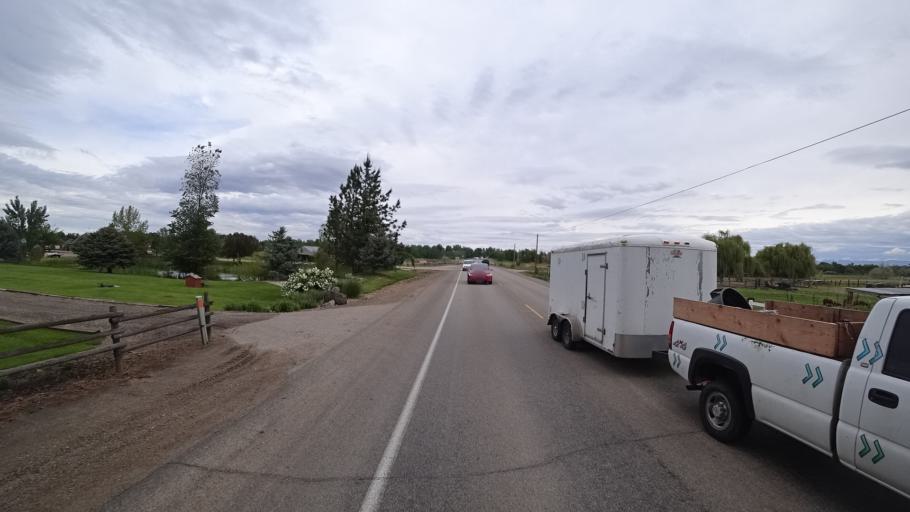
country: US
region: Idaho
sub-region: Ada County
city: Star
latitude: 43.6762
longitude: -116.4934
